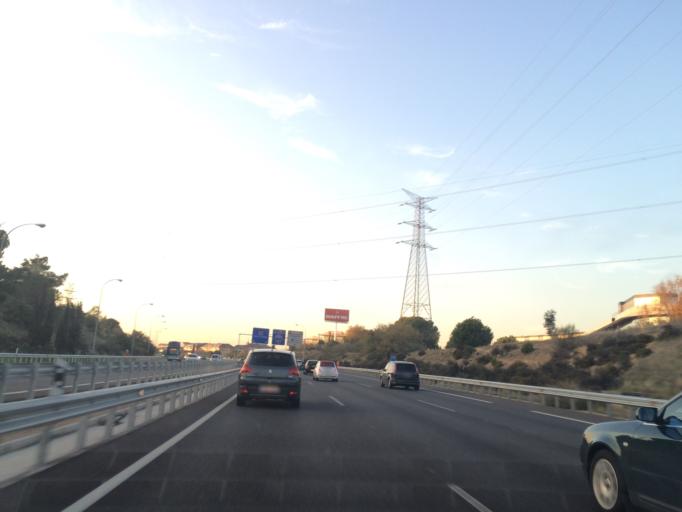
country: ES
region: Madrid
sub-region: Provincia de Madrid
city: Majadahonda
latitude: 40.4462
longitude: -3.8536
